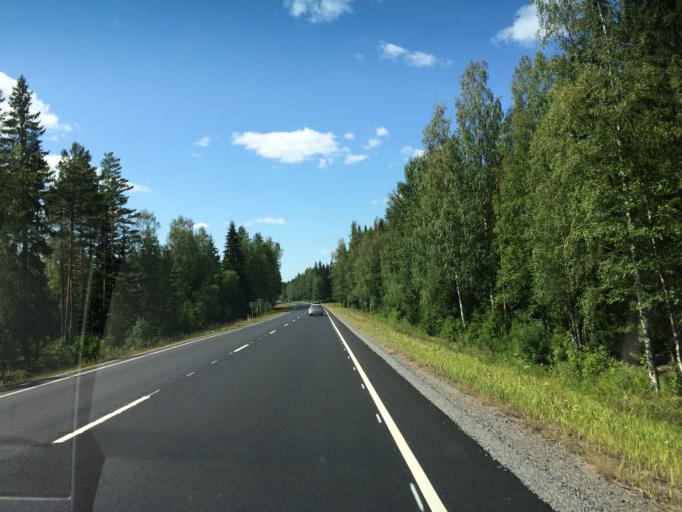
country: FI
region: Pirkanmaa
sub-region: Lounais-Pirkanmaa
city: Kiikoinen
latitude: 61.4756
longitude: 22.4627
